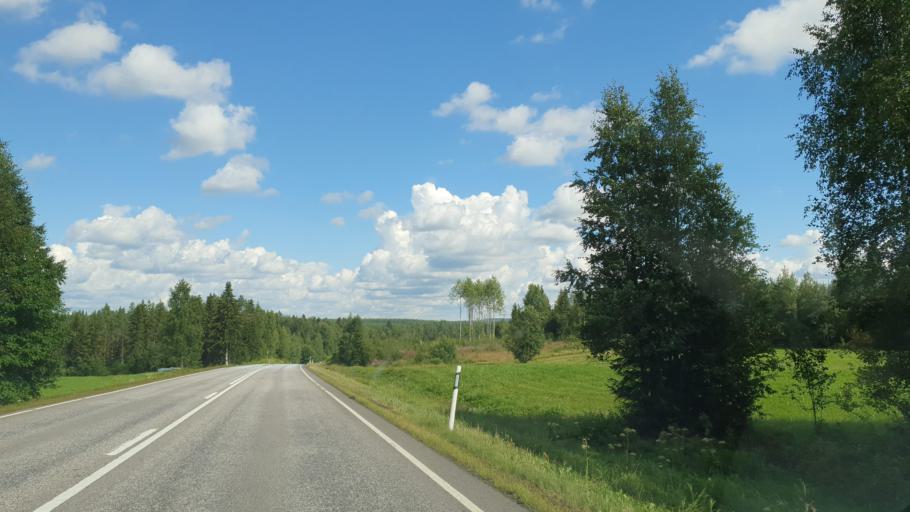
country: FI
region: Northern Savo
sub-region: Ylae-Savo
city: Sonkajaervi
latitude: 63.7535
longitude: 27.3895
